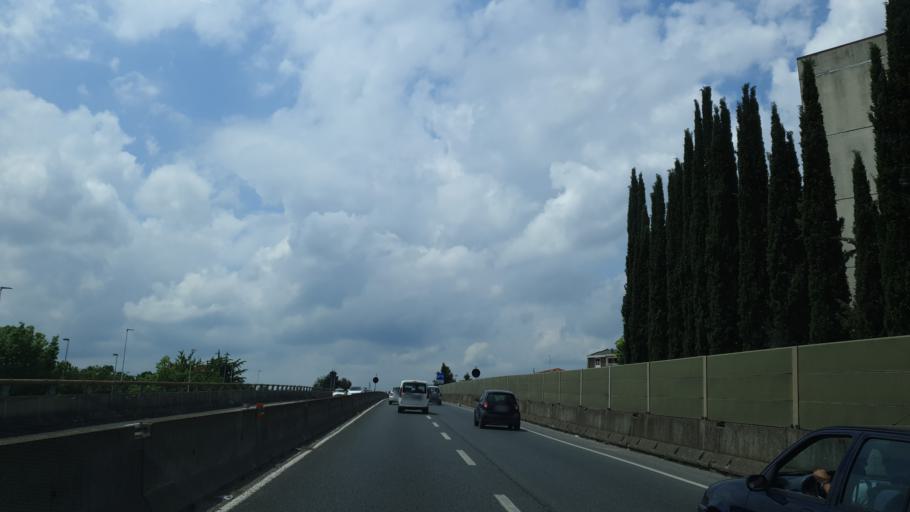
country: IT
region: Tuscany
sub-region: Province of Florence
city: Scandicci
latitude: 43.7719
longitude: 11.1933
